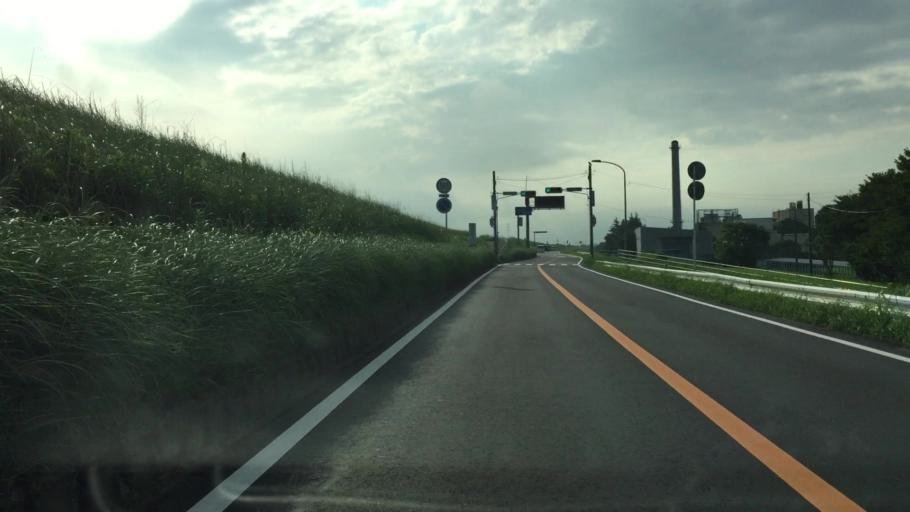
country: JP
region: Ibaraki
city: Toride
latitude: 35.8802
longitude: 140.0918
